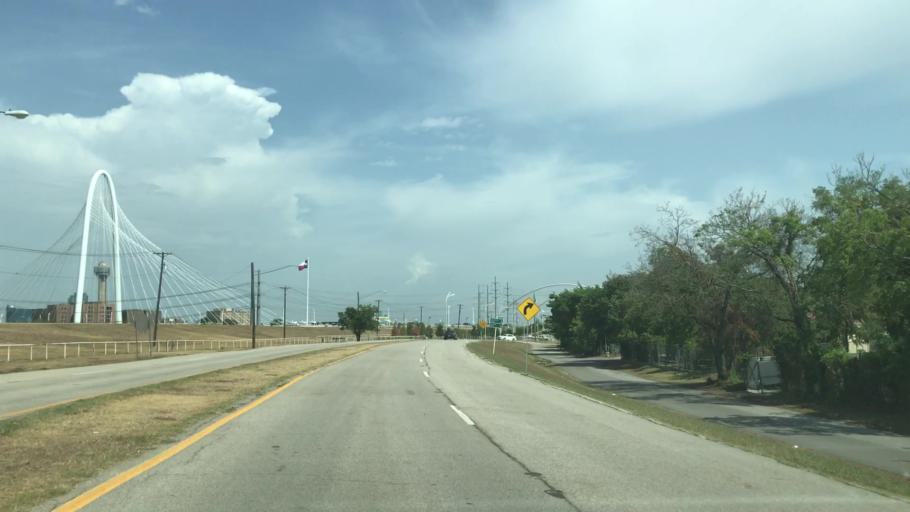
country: US
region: Texas
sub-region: Dallas County
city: Dallas
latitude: 32.7825
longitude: -96.8291
